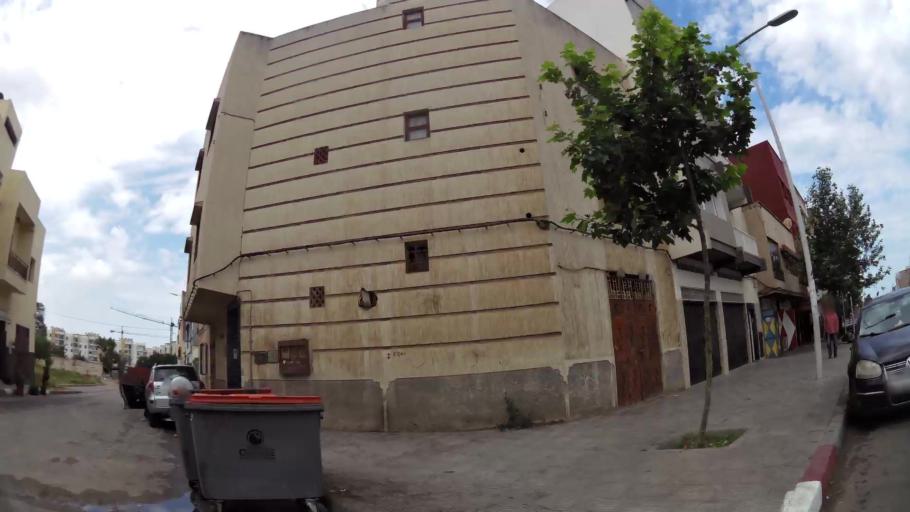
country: MA
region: Rabat-Sale-Zemmour-Zaer
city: Sale
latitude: 34.0379
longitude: -6.8079
